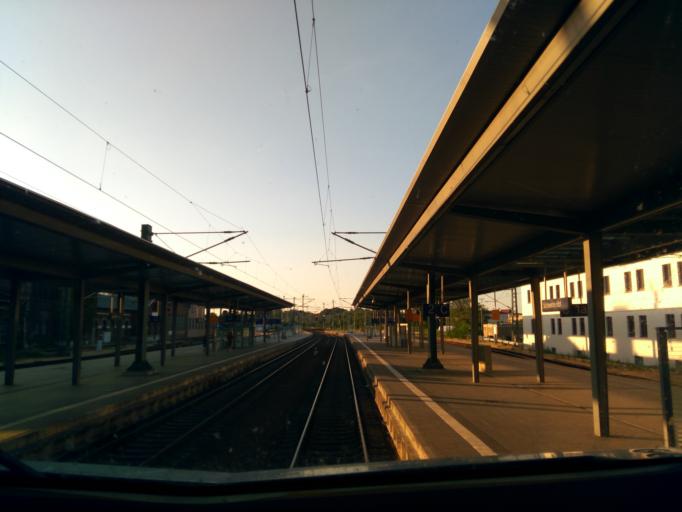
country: DE
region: Mecklenburg-Vorpommern
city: Paulsstadt
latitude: 53.6345
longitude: 11.4075
